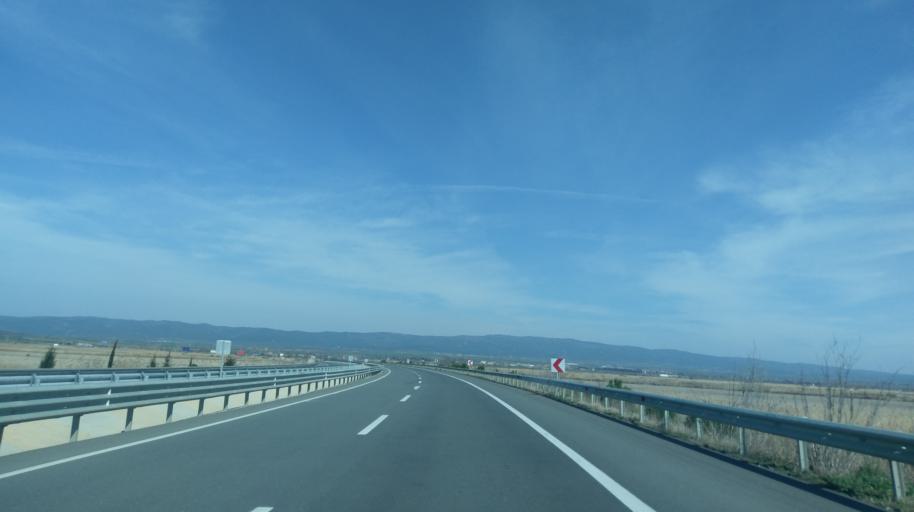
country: TR
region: Canakkale
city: Evrese
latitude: 40.6279
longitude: 26.8689
